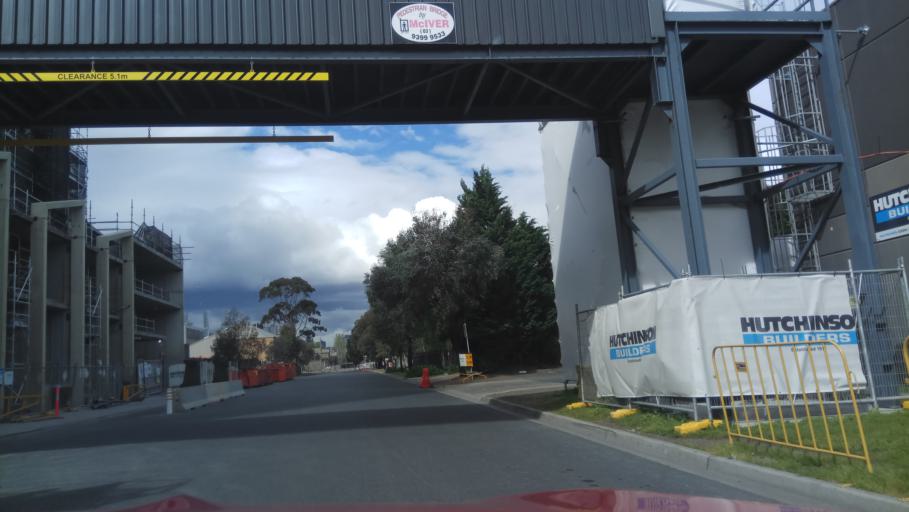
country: AU
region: Victoria
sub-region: Port Phillip
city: Port Melbourne
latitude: -37.8347
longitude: 144.9201
